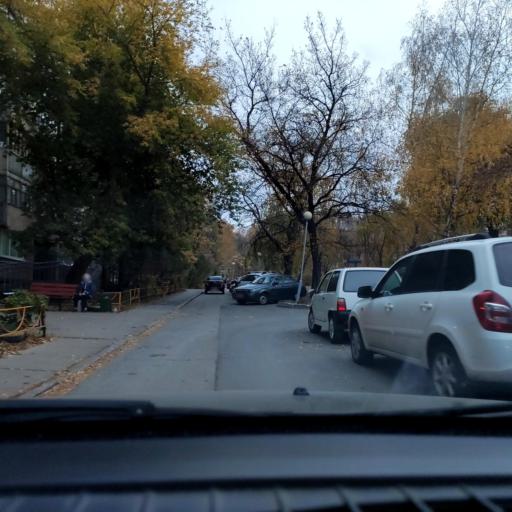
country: RU
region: Samara
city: Tol'yatti
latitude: 53.5201
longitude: 49.2662
